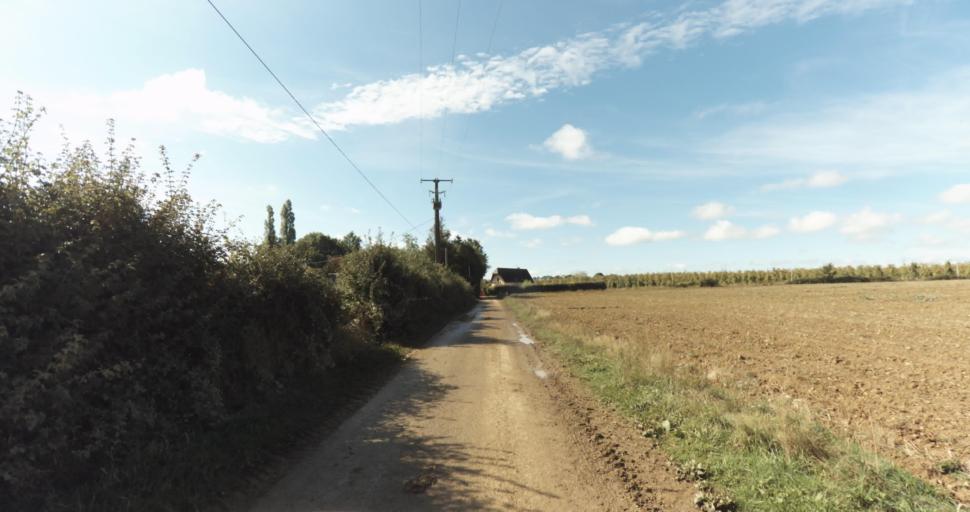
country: FR
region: Lower Normandy
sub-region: Departement du Calvados
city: Orbec
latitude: 48.9278
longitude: 0.3586
